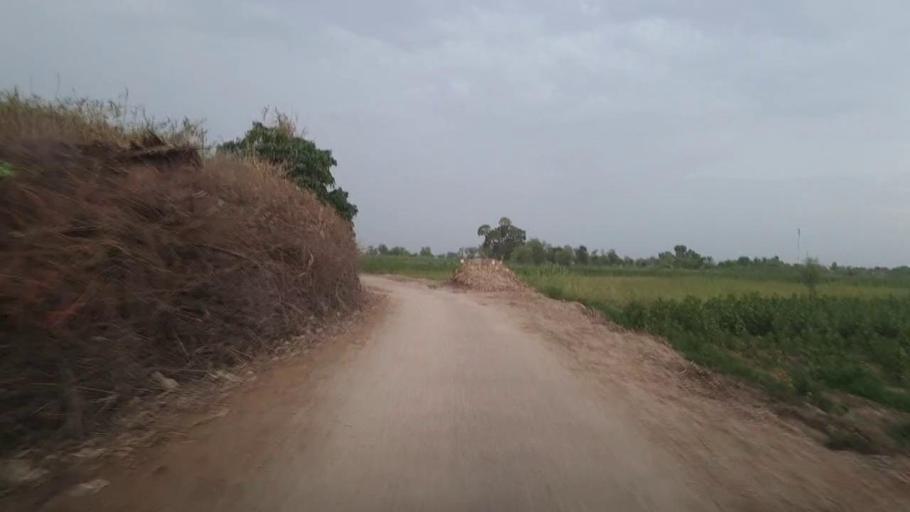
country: PK
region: Sindh
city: Karaundi
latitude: 27.0085
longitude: 68.3430
